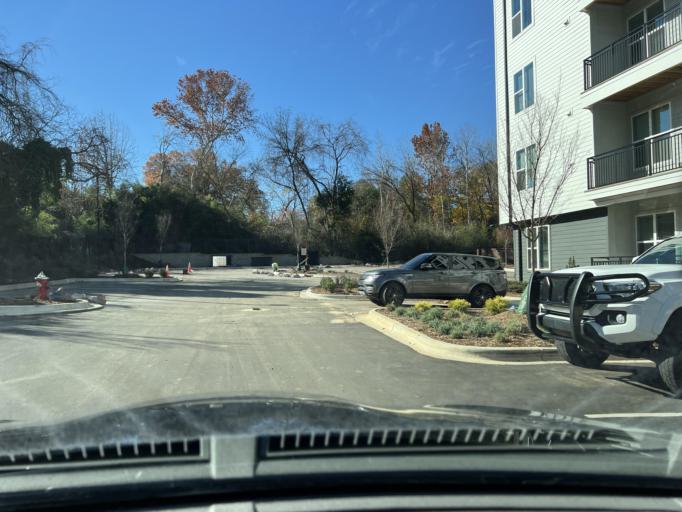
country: US
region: North Carolina
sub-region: Wake County
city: Raleigh
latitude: 35.8184
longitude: -78.5987
